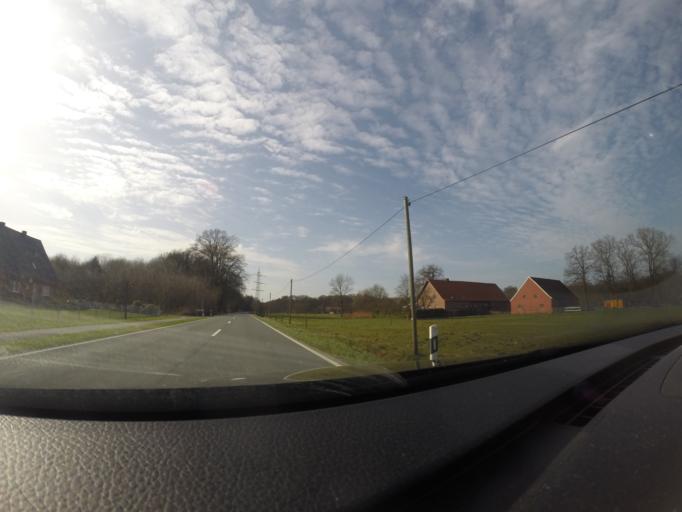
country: DE
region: North Rhine-Westphalia
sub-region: Regierungsbezirk Munster
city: Legden
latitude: 52.0279
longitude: 7.0818
